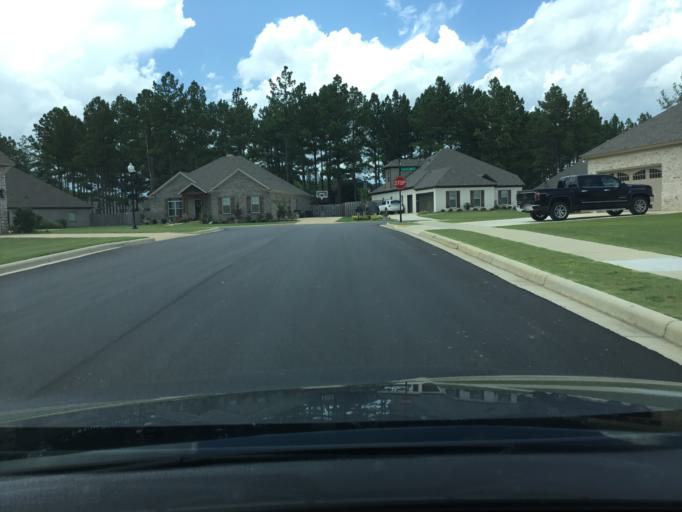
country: US
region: Alabama
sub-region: Montgomery County
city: Pike Road
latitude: 32.3370
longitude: -86.0799
